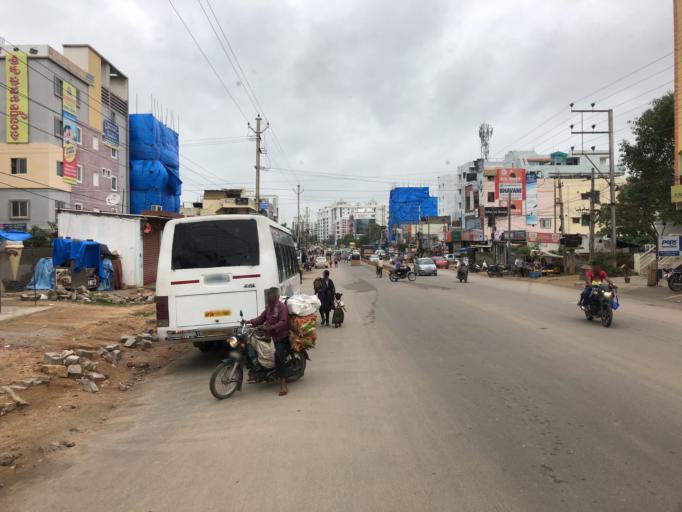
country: IN
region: Telangana
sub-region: Medak
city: Serilingampalle
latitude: 17.4608
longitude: 78.3536
